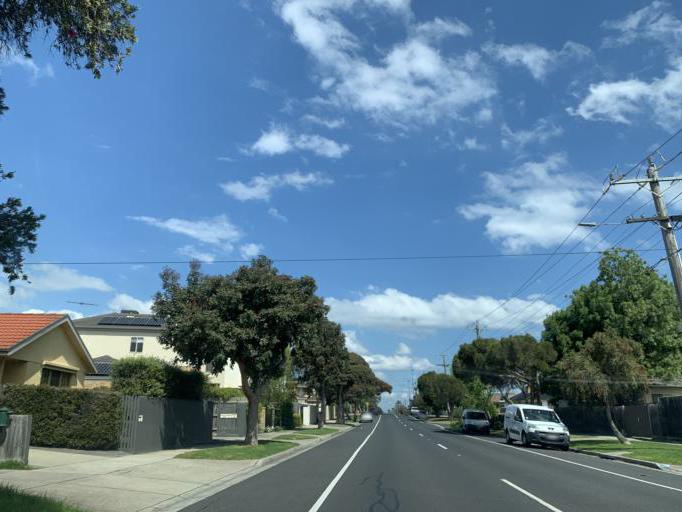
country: AU
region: Victoria
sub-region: Kingston
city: Mordialloc
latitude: -38.0000
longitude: 145.0940
